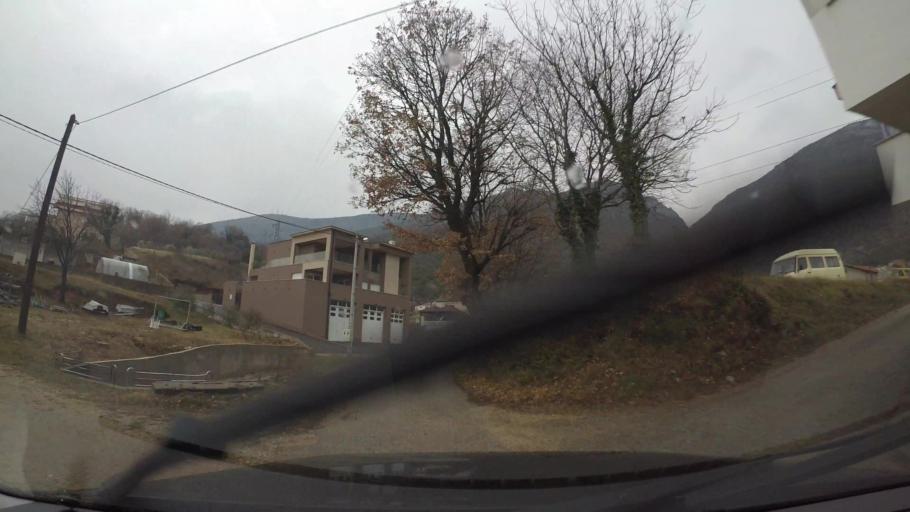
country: BA
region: Federation of Bosnia and Herzegovina
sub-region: Hercegovacko-Bosanski Kanton
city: Mostar
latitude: 43.3682
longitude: 17.8084
